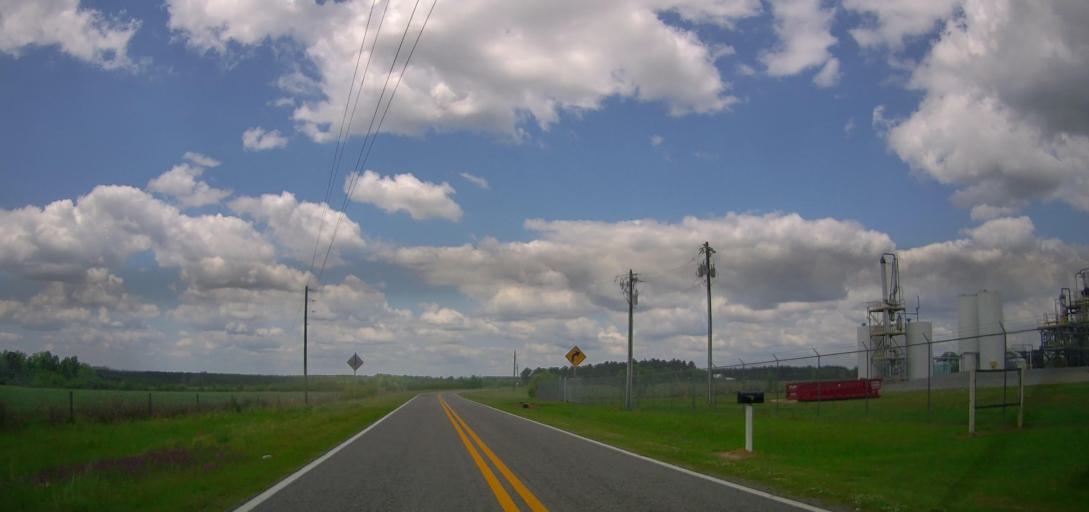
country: US
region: Georgia
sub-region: Laurens County
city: East Dublin
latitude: 32.5431
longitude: -82.8169
